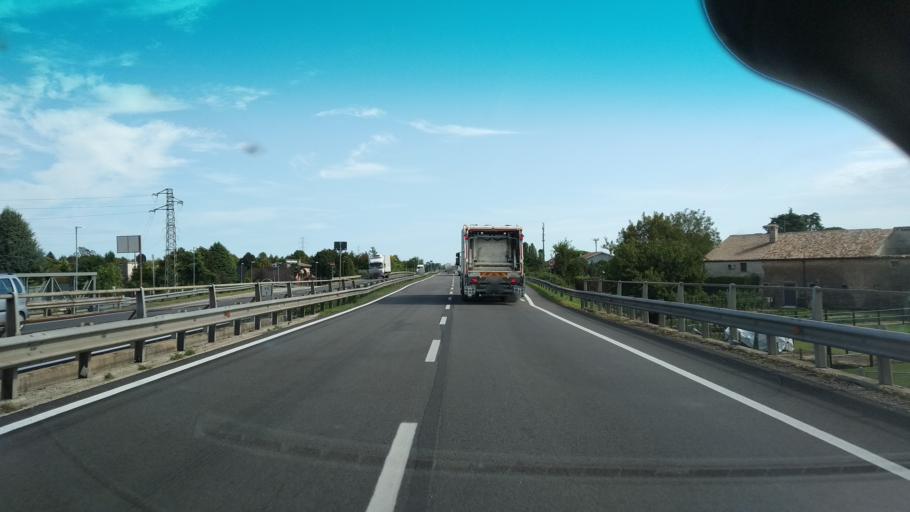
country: IT
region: Veneto
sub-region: Provincia di Padova
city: Villatora
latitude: 45.3798
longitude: 11.9740
